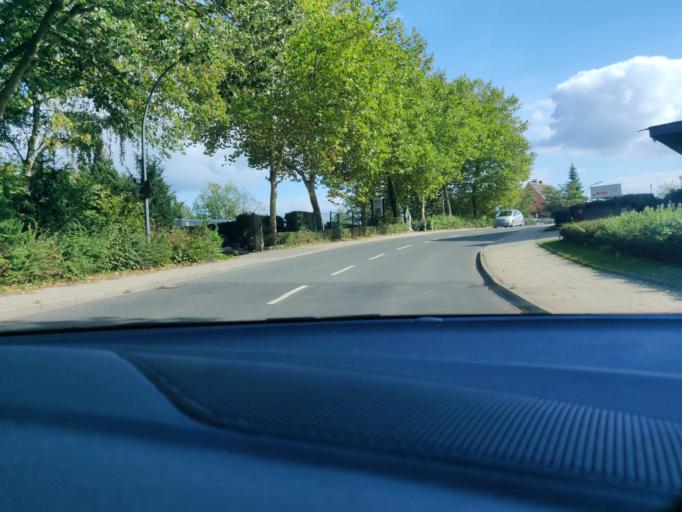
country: DE
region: North Rhine-Westphalia
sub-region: Regierungsbezirk Dusseldorf
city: Velbert
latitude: 51.3399
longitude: 7.0253
